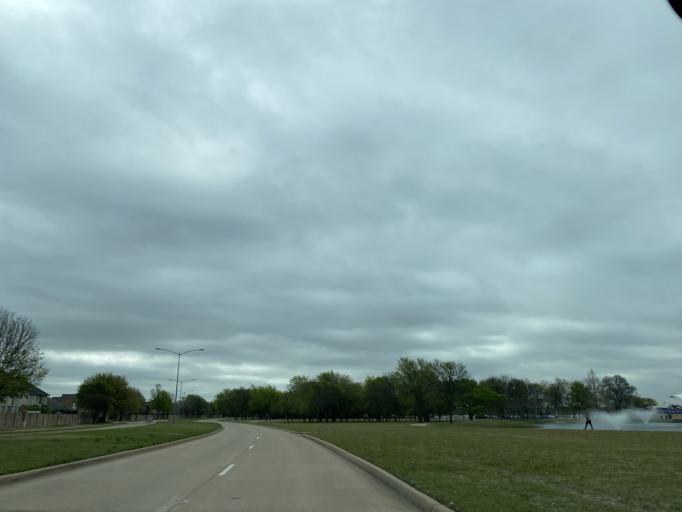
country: US
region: Texas
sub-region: Collin County
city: Allen
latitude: 33.1099
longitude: -96.6255
